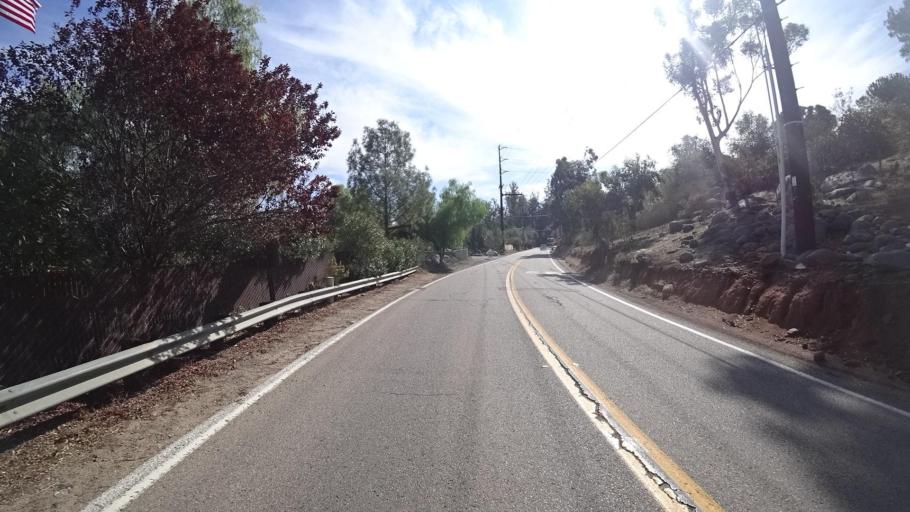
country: US
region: California
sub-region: San Diego County
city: Alpine
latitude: 32.8296
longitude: -116.7901
